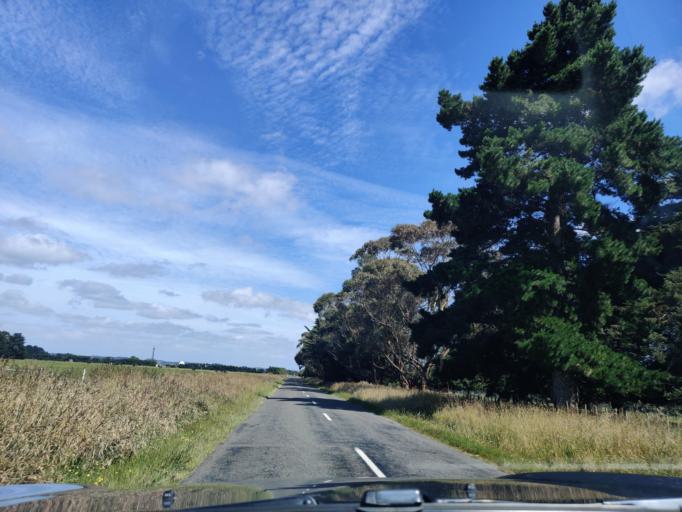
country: NZ
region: Manawatu-Wanganui
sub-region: Rangitikei District
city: Bulls
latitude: -40.1827
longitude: 175.4390
